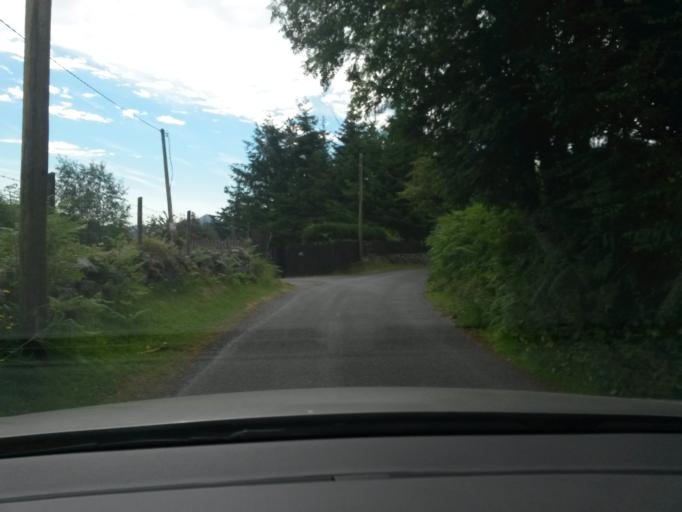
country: IE
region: Leinster
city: Ballinteer
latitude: 53.1797
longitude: -6.2648
